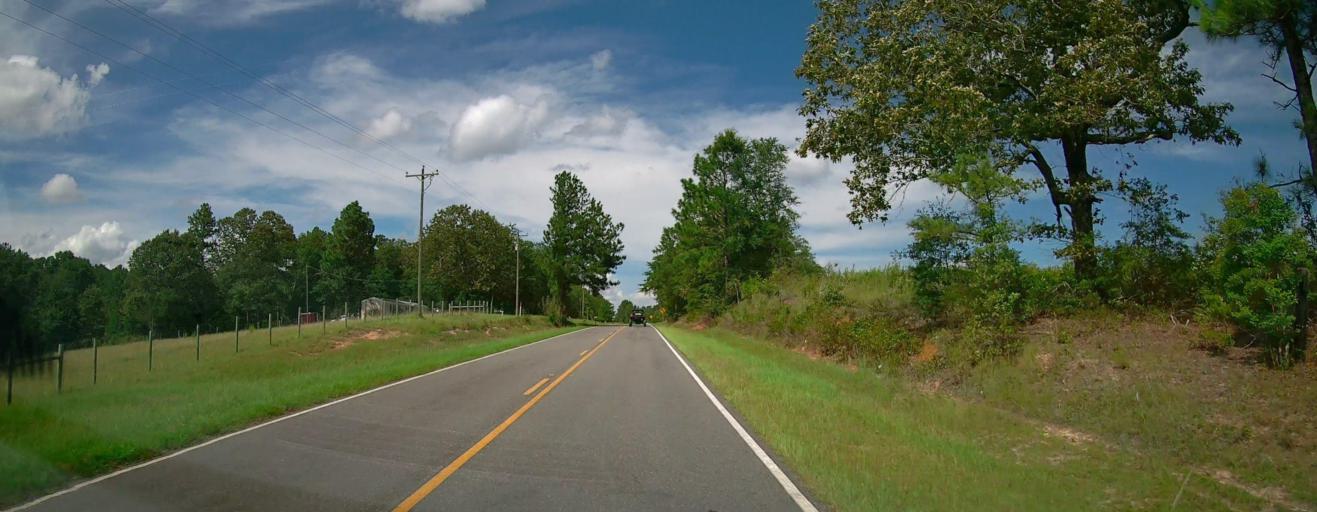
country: US
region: Georgia
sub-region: Taylor County
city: Butler
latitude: 32.4539
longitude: -84.1958
